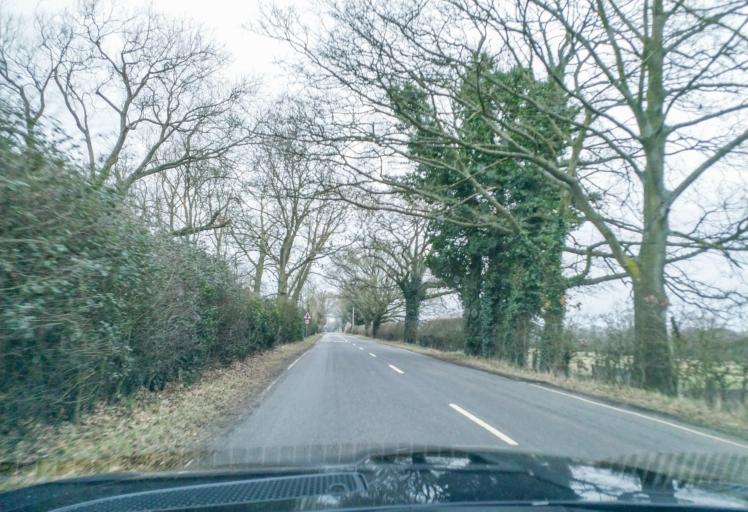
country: GB
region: England
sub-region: Warwickshire
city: Wroxall
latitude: 52.3098
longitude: -1.6800
